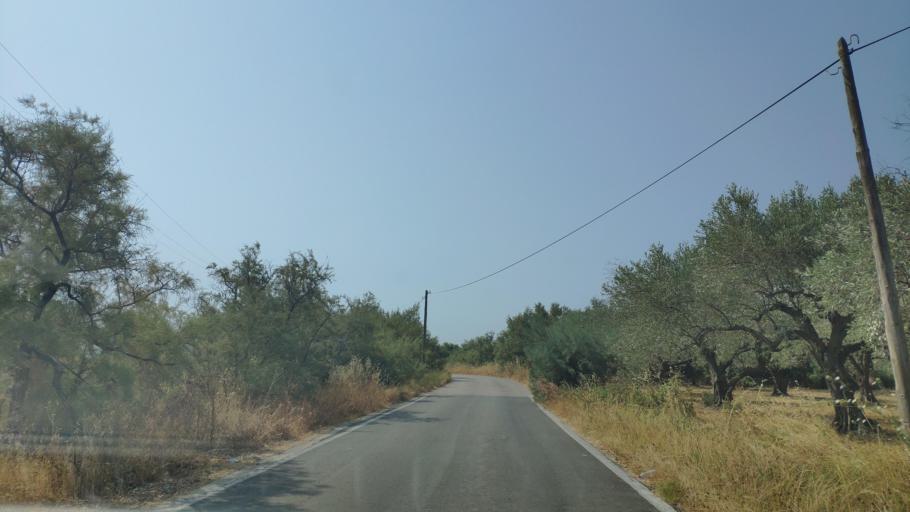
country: GR
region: West Greece
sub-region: Nomos Aitolias kai Akarnanias
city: Menidi
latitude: 39.0436
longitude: 21.0727
